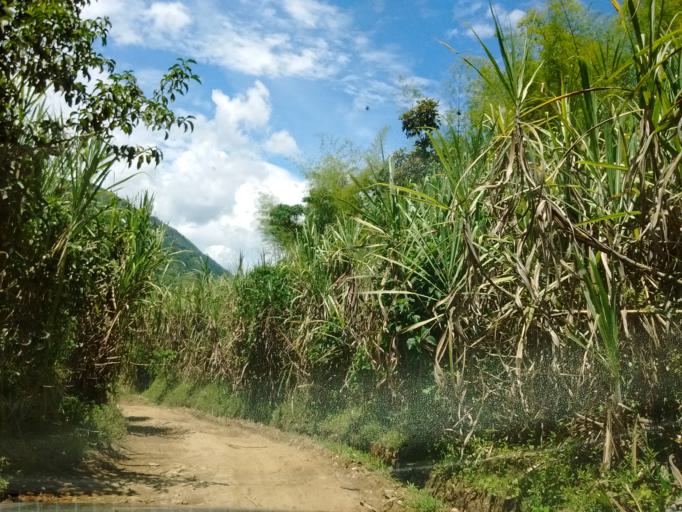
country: CO
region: Cauca
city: Villa Rica
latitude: 2.6302
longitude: -76.7719
